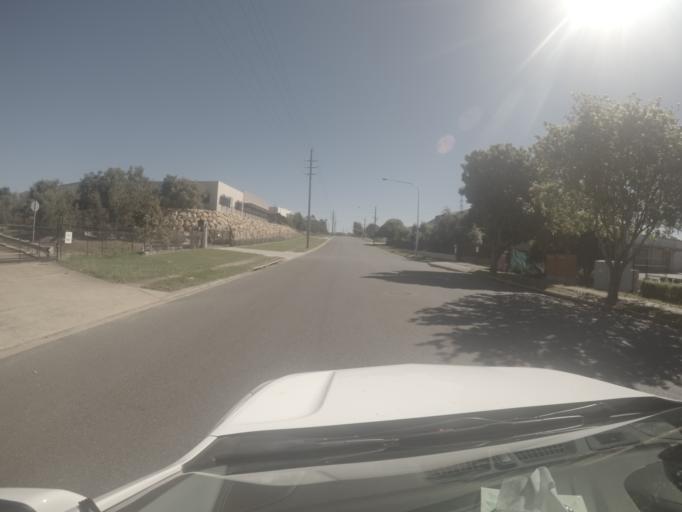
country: AU
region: Queensland
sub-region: Brisbane
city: Richlands
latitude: -27.5800
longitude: 152.9512
